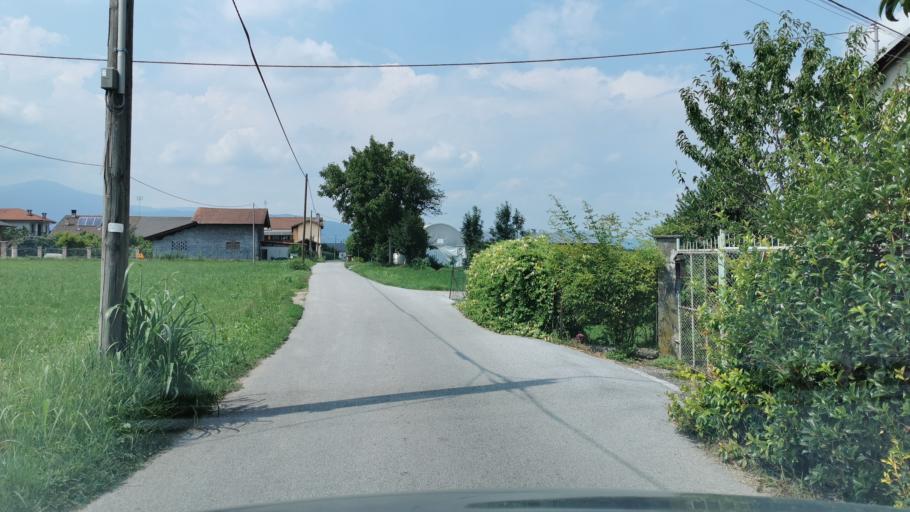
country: IT
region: Piedmont
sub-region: Provincia di Cuneo
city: Caraglio
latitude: 44.4264
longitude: 7.4522
